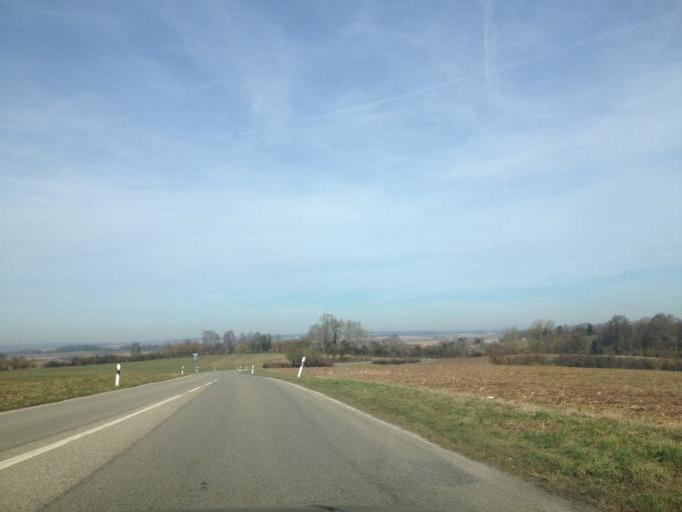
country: DE
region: Baden-Wuerttemberg
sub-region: Regierungsbezirk Stuttgart
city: Oedheim
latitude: 49.2130
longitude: 9.2757
